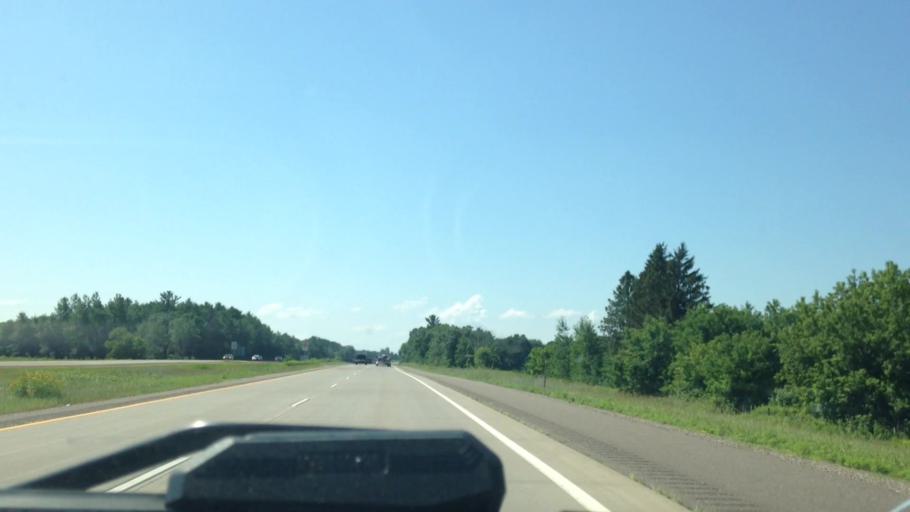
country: US
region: Wisconsin
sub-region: Barron County
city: Cameron
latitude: 45.4534
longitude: -91.7604
